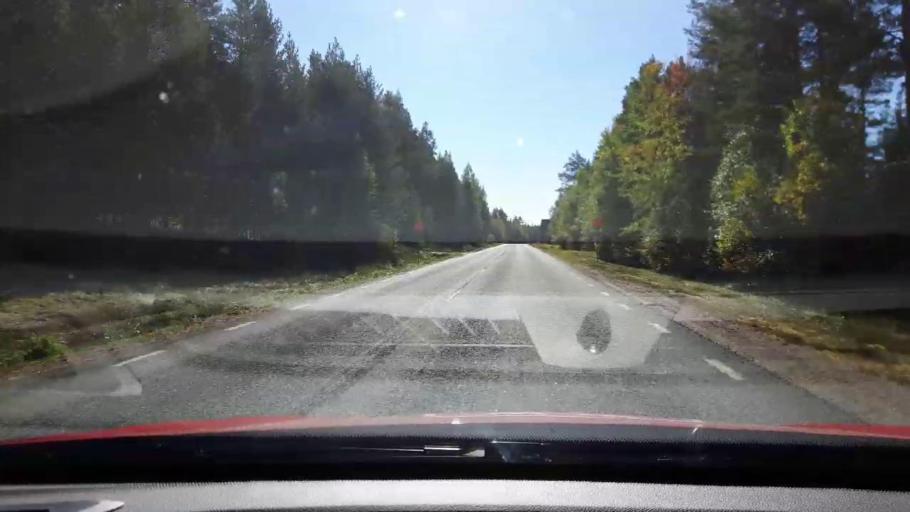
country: SE
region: Jaemtland
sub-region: Harjedalens Kommun
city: Sveg
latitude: 62.3284
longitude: 14.0592
